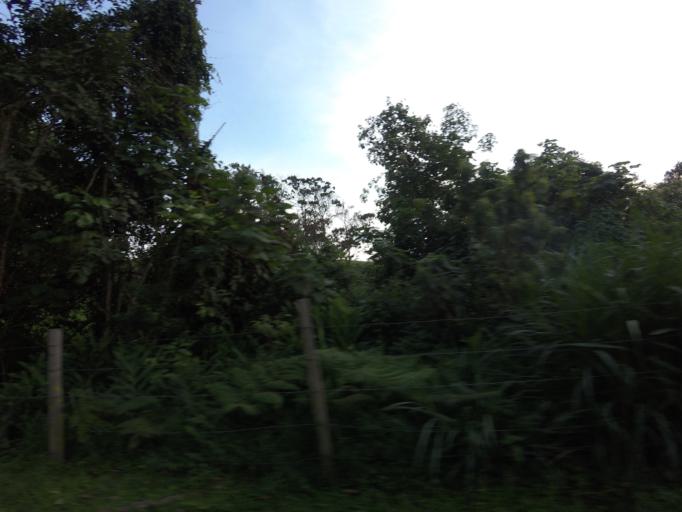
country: CO
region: Cundinamarca
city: Zipacon
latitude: 4.7592
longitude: -74.4381
